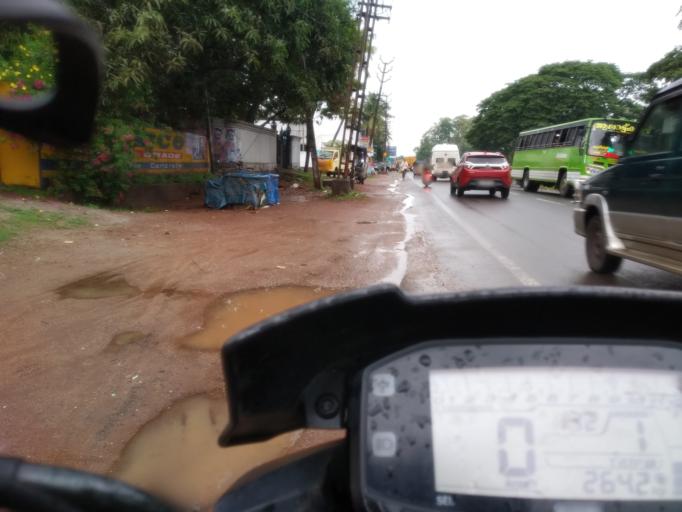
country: IN
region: Kerala
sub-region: Kollam
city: Kollam
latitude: 8.8669
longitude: 76.6478
